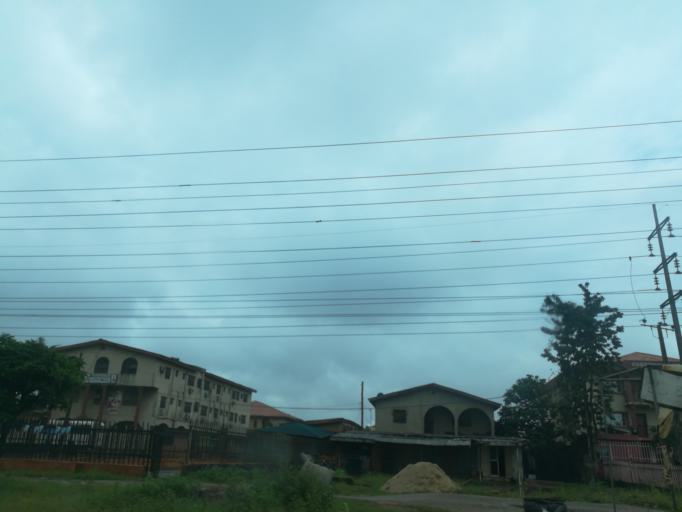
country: NG
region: Lagos
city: Ikorodu
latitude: 6.6370
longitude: 3.5131
